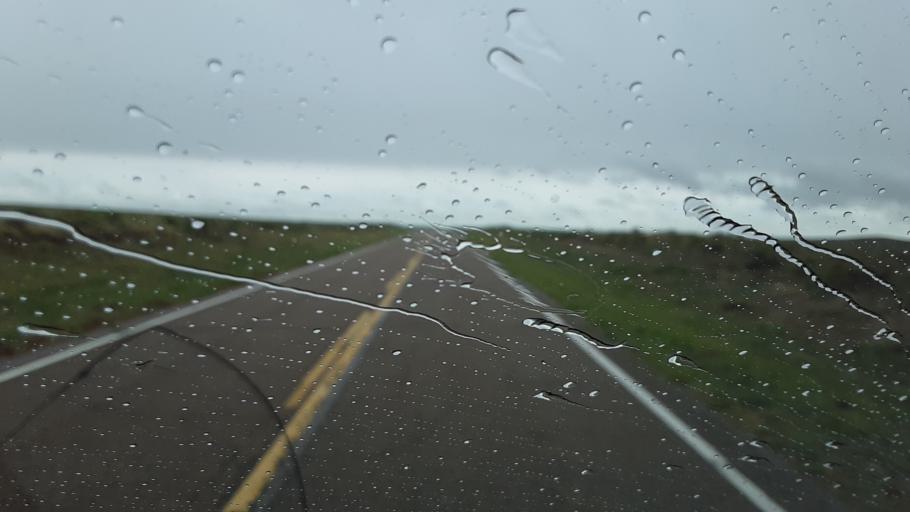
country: US
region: Colorado
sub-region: Lincoln County
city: Hugo
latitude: 38.8494
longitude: -103.2354
